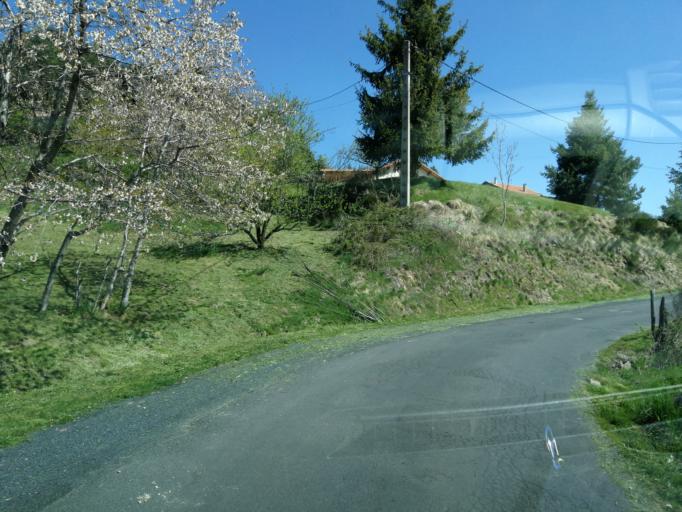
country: FR
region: Rhone-Alpes
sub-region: Departement de l'Ardeche
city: Le Cheylard
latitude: 44.9408
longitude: 4.4280
